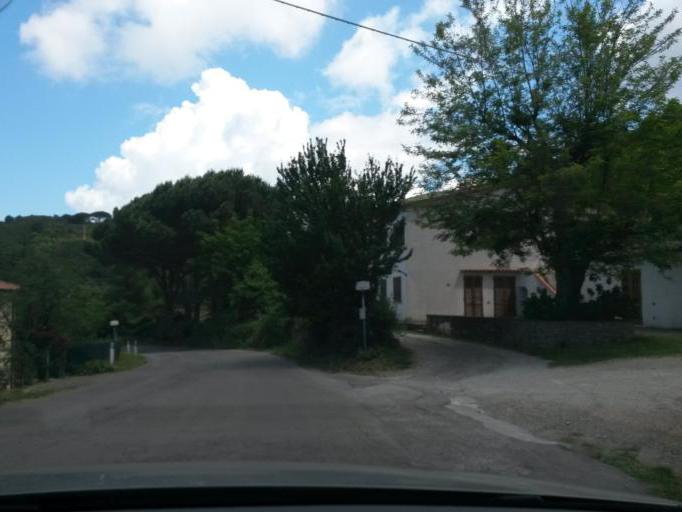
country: IT
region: Tuscany
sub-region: Provincia di Livorno
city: Marciana Marina
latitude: 42.7928
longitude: 10.1891
